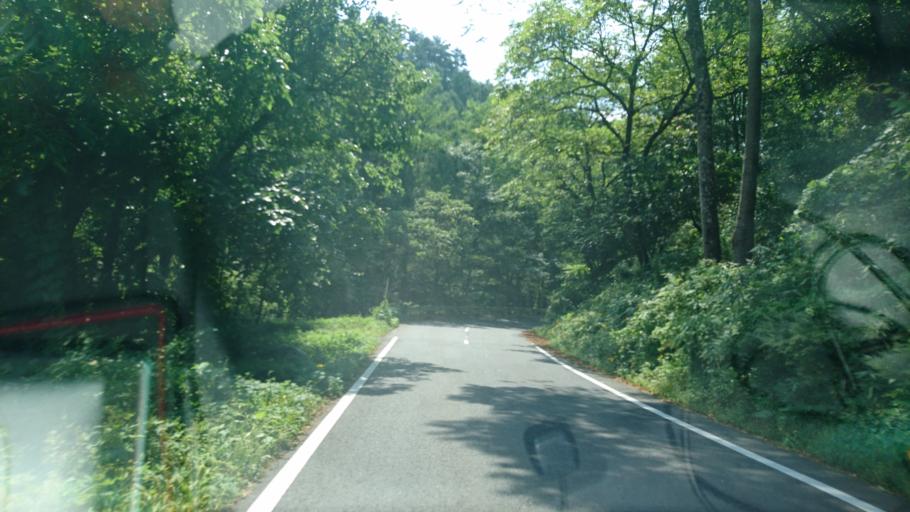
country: JP
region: Gunma
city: Numata
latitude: 36.7421
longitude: 139.2372
